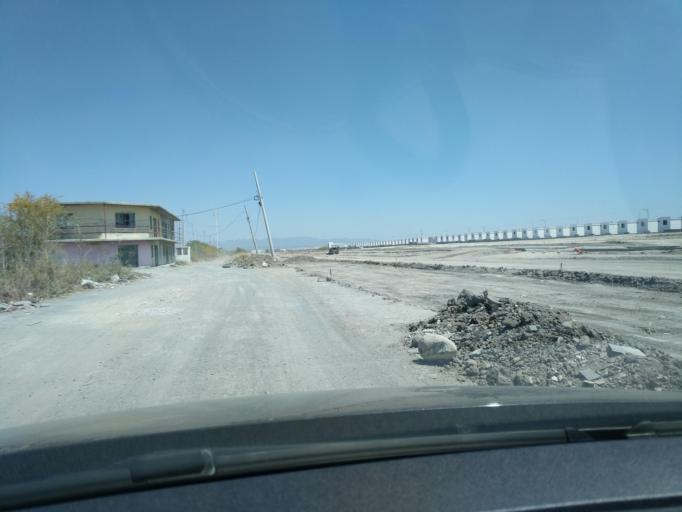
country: MX
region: Nuevo Leon
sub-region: Salinas Victoria
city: Emiliano Zapata
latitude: 25.9117
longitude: -100.2634
